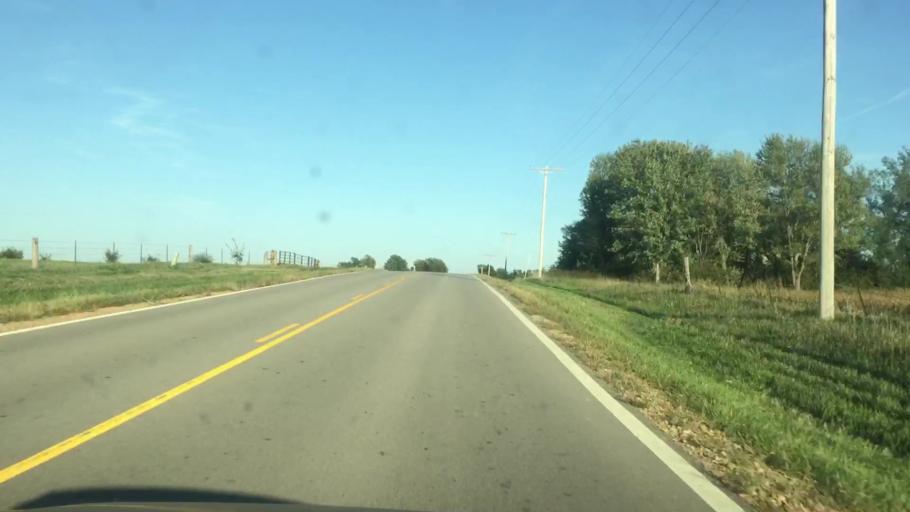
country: US
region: Kansas
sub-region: Brown County
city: Horton
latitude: 39.5876
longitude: -95.5939
